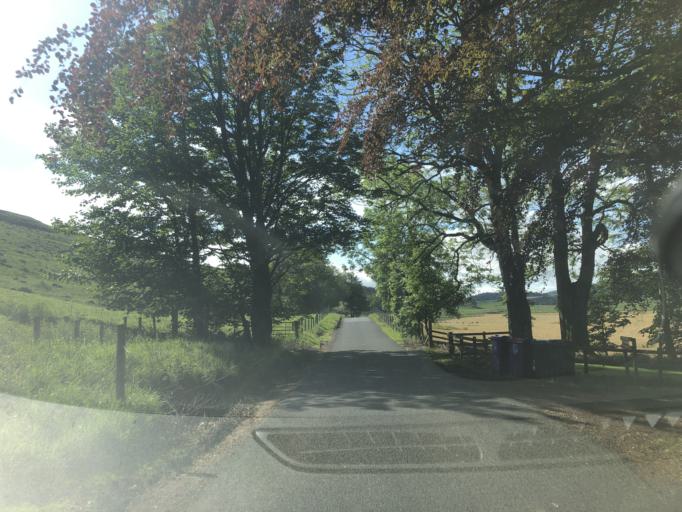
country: GB
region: Scotland
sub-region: Angus
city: Kirriemuir
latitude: 56.7916
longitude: -3.0329
